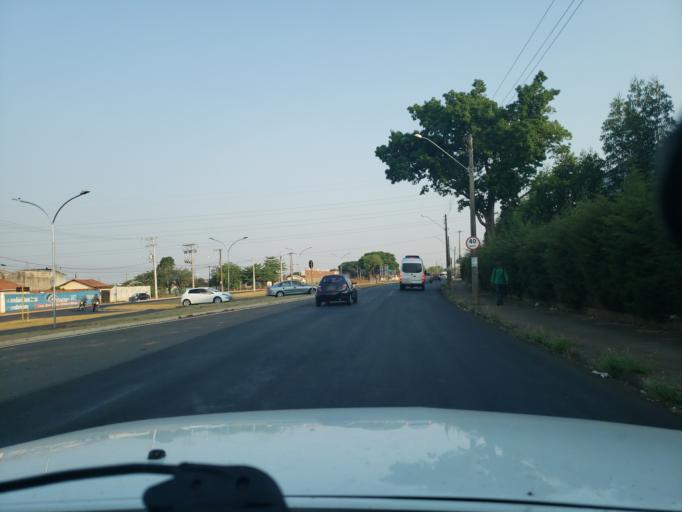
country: BR
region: Sao Paulo
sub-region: Moji-Guacu
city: Mogi-Gaucu
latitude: -22.3385
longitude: -46.9436
